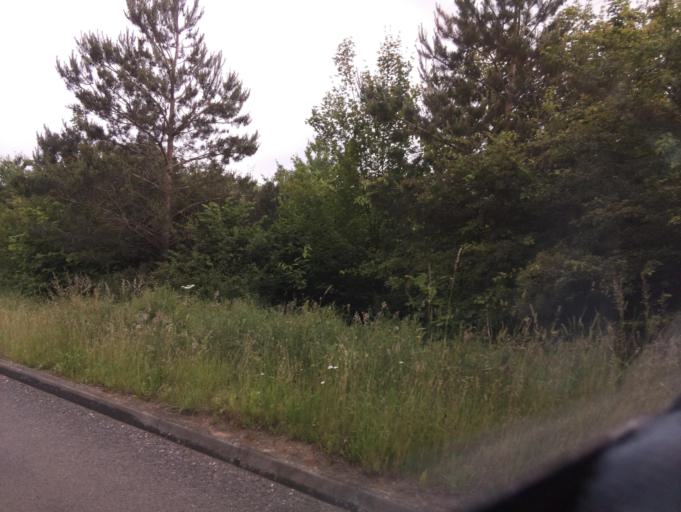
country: GB
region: England
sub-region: District of Rutland
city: Oakham
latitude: 52.6658
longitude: -0.7132
